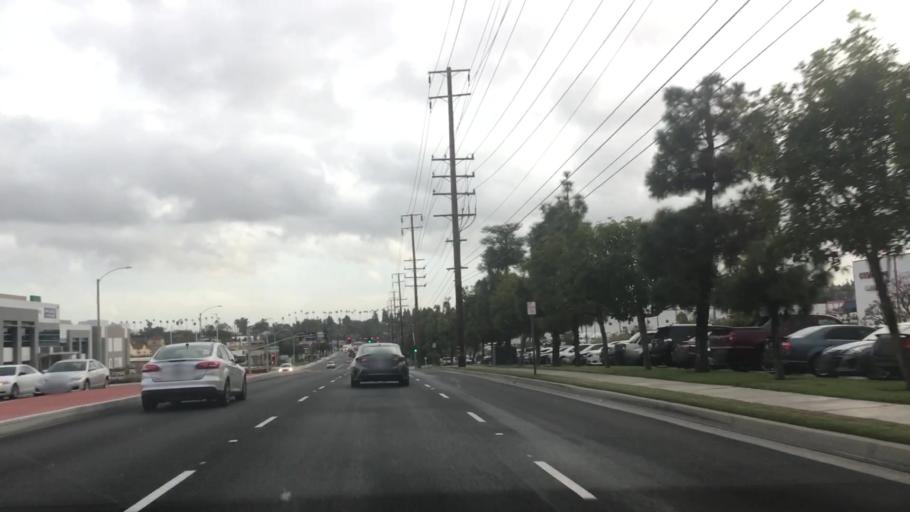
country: US
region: California
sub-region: Orange County
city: La Habra
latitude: 33.9226
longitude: -117.9332
